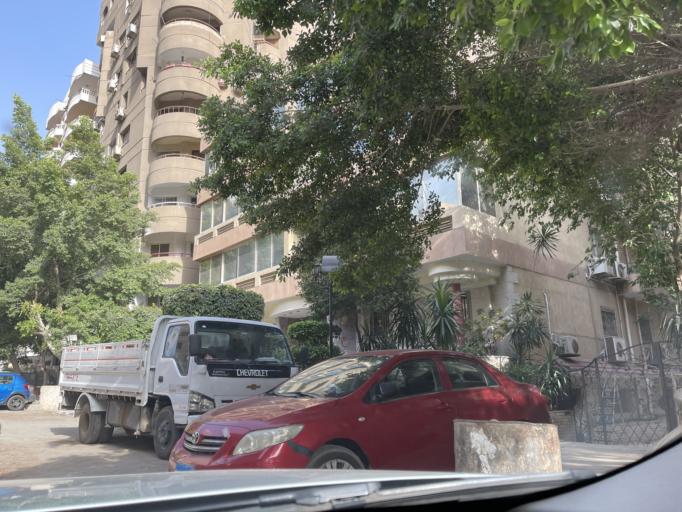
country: EG
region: Muhafazat al Qahirah
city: Cairo
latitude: 30.0674
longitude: 31.3538
